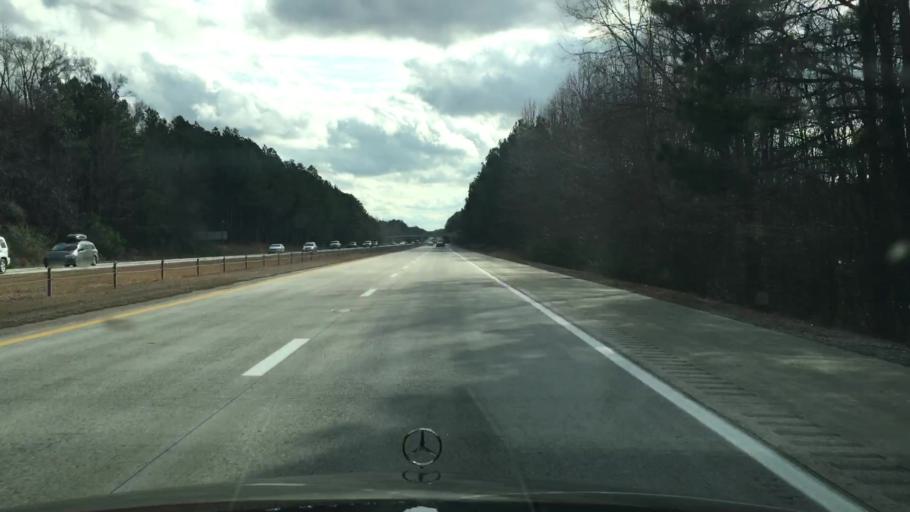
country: US
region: North Carolina
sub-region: Johnston County
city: Benson
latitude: 35.4959
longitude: -78.5534
